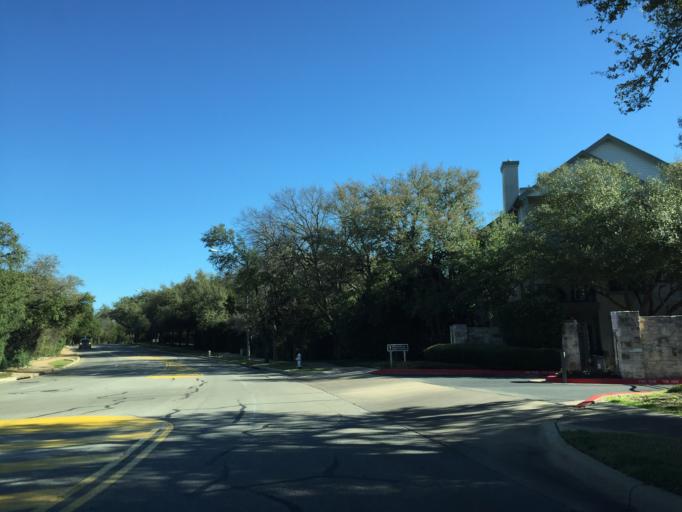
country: US
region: Texas
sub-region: Williamson County
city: Jollyville
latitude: 30.4301
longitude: -97.7477
